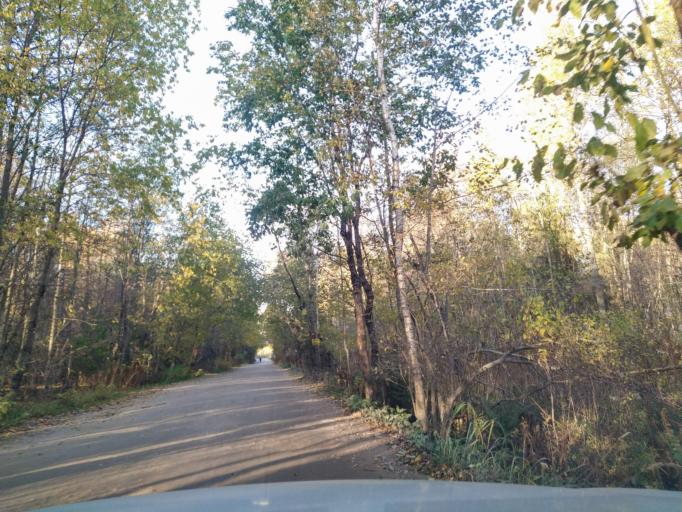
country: RU
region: Leningrad
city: Siverskiy
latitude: 59.2972
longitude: 30.0343
